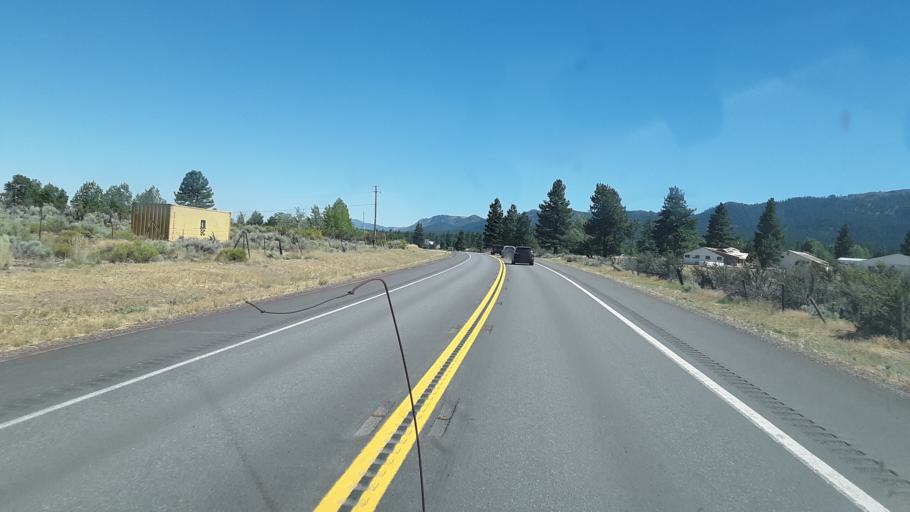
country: US
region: California
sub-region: Lassen County
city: Janesville
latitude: 40.3187
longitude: -120.5432
